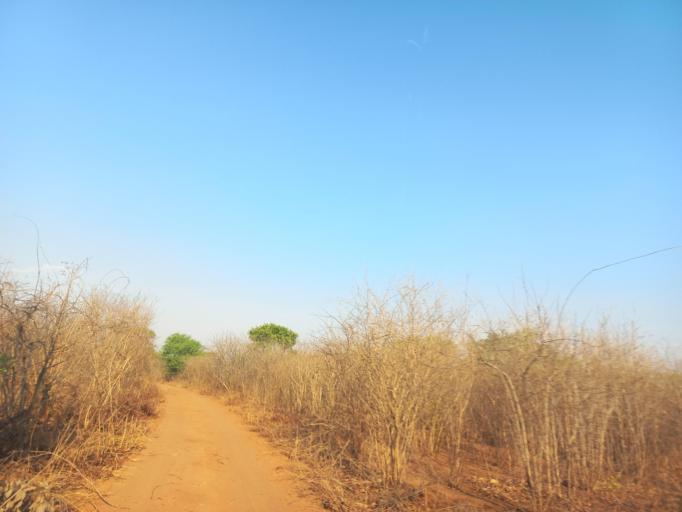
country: ZM
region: Lusaka
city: Luangwa
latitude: -15.4212
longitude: 30.2685
